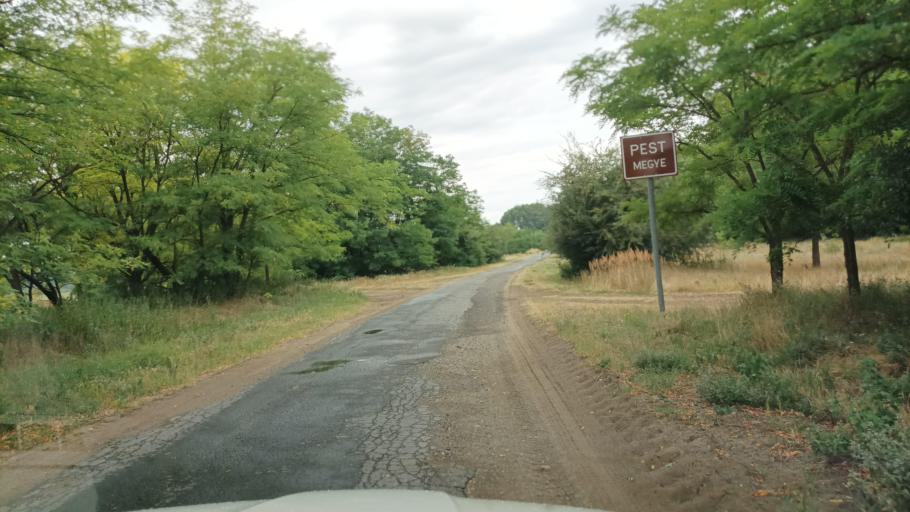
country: HU
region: Pest
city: Orkeny
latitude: 47.0274
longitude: 19.3679
